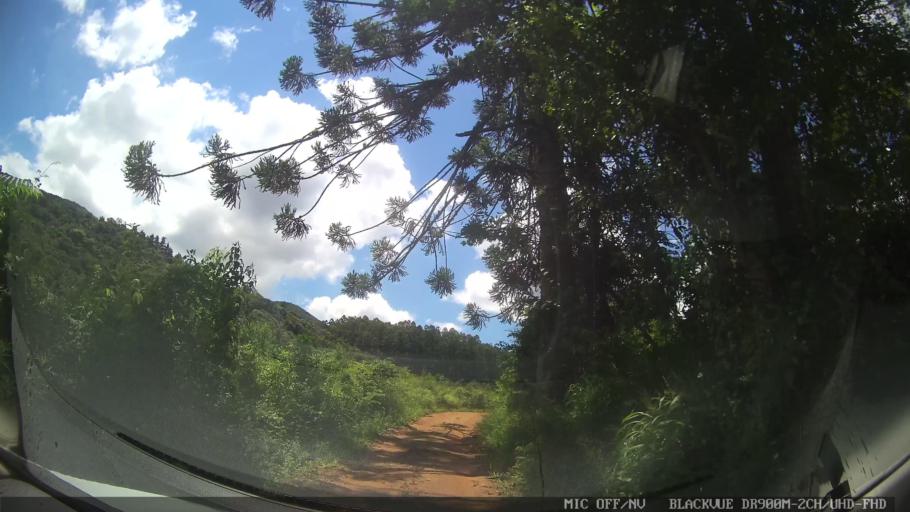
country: BR
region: Minas Gerais
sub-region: Extrema
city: Extrema
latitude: -22.8904
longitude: -46.2961
